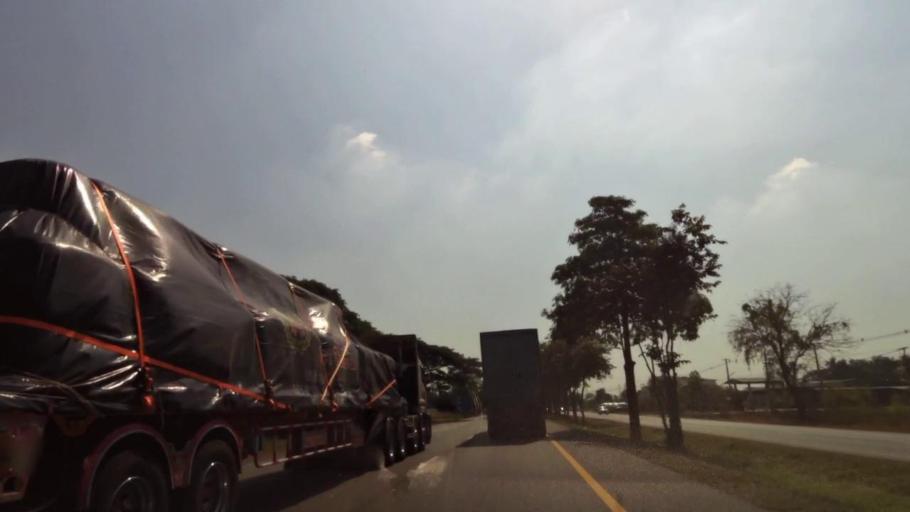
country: TH
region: Phichit
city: Bueng Na Rang
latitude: 16.1346
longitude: 100.1255
